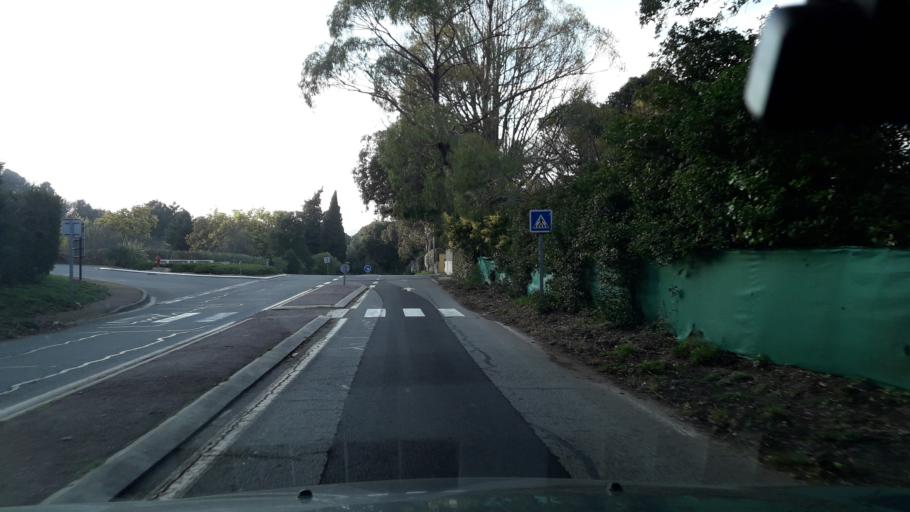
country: FR
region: Provence-Alpes-Cote d'Azur
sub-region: Departement du Var
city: Tanneron
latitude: 43.5188
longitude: 6.8462
